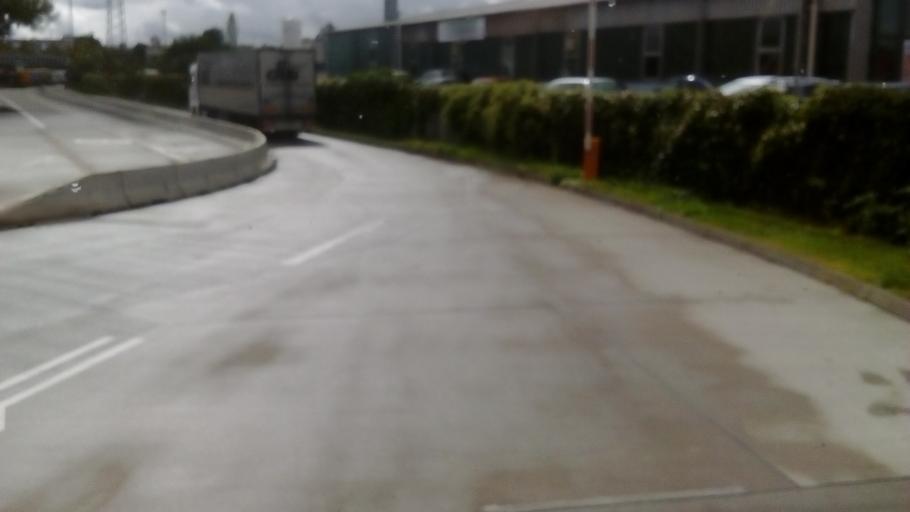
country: DE
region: Baden-Wuerttemberg
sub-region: Freiburg Region
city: Weil am Rhein
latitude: 47.5980
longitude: 7.6014
